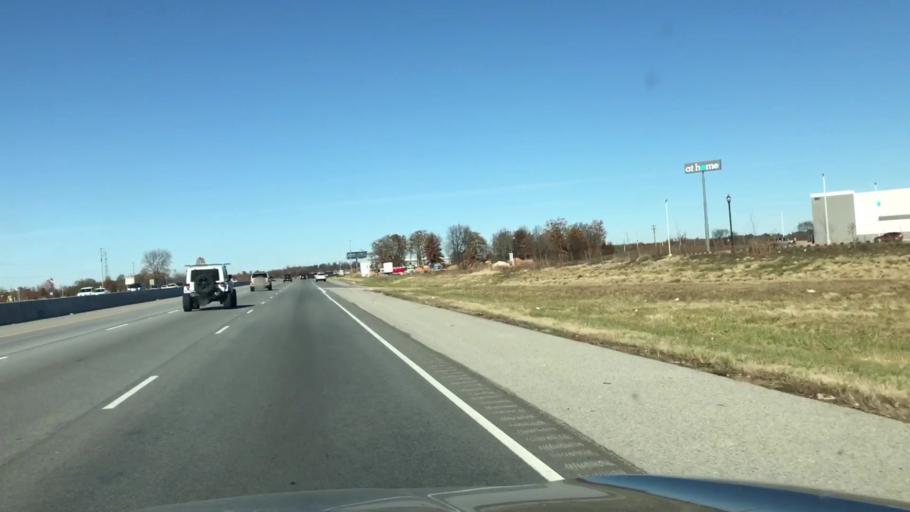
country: US
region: Arkansas
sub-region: Benton County
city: Lowell
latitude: 36.2850
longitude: -94.1575
